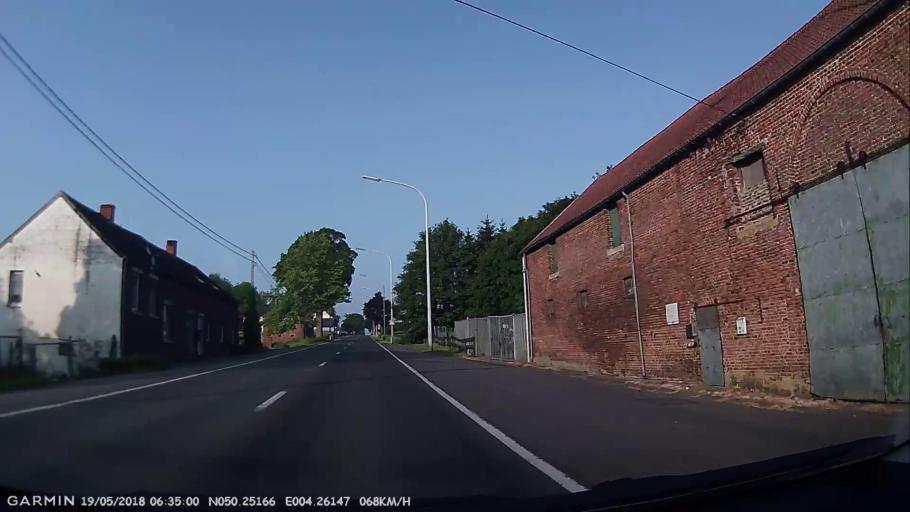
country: BE
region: Wallonia
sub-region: Province du Hainaut
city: Beaumont
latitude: 50.2515
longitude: 4.2613
